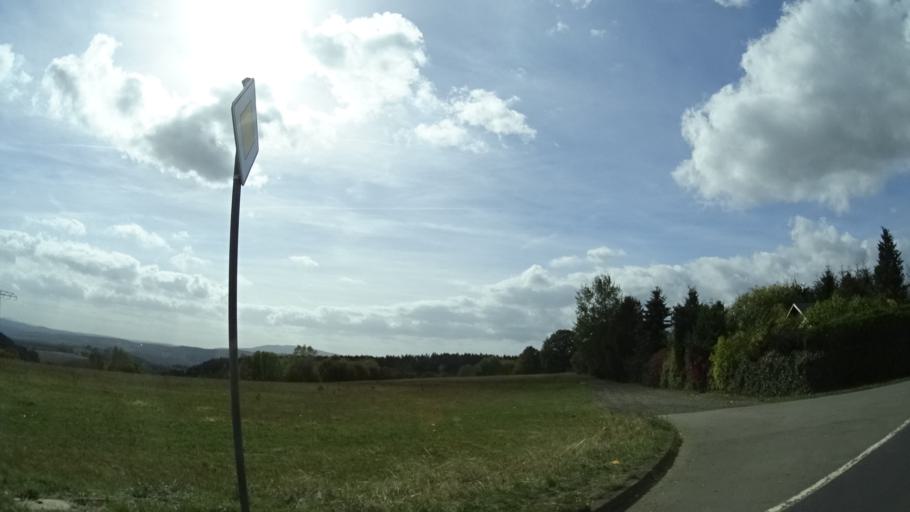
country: DE
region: Thuringia
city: Rotterode
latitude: 50.7143
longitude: 10.5459
